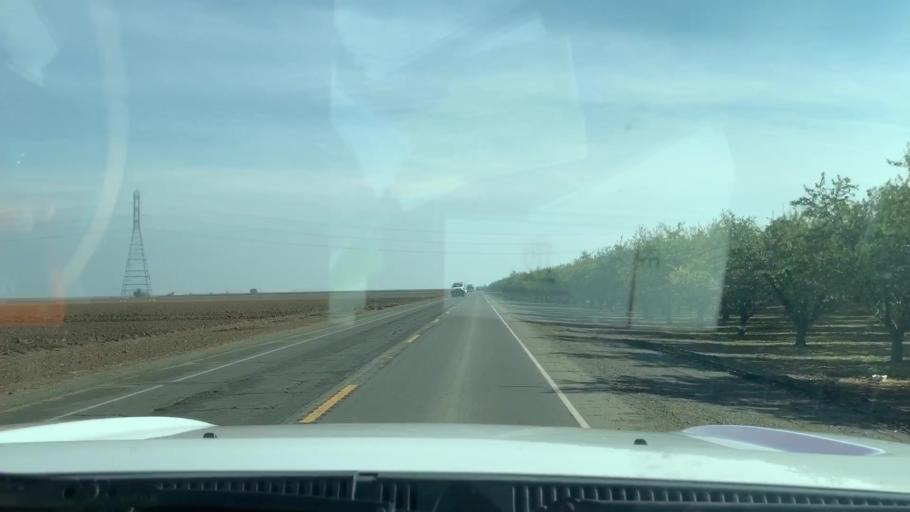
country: US
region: California
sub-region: Fresno County
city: Huron
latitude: 36.2547
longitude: -120.2193
